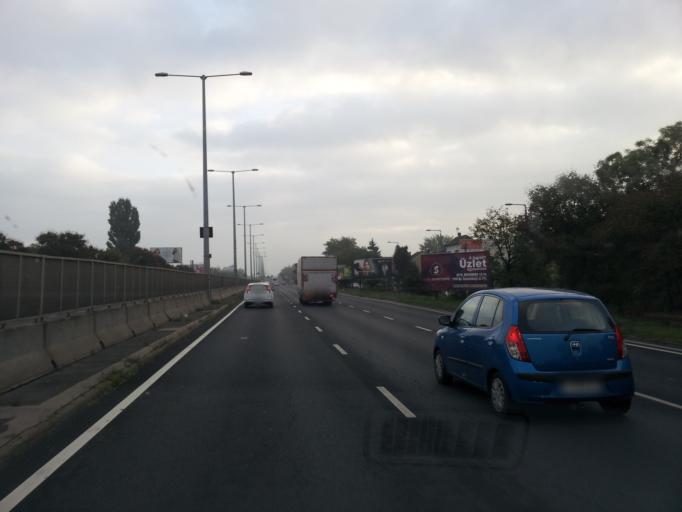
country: HU
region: Budapest
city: Budapest XV. keruelet
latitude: 47.5515
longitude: 19.1249
